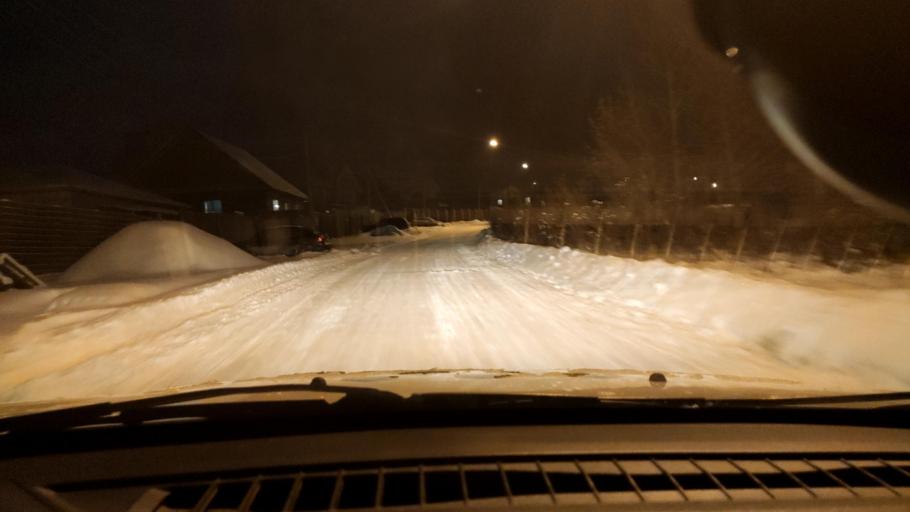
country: RU
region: Perm
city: Perm
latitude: 58.0275
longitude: 56.3443
